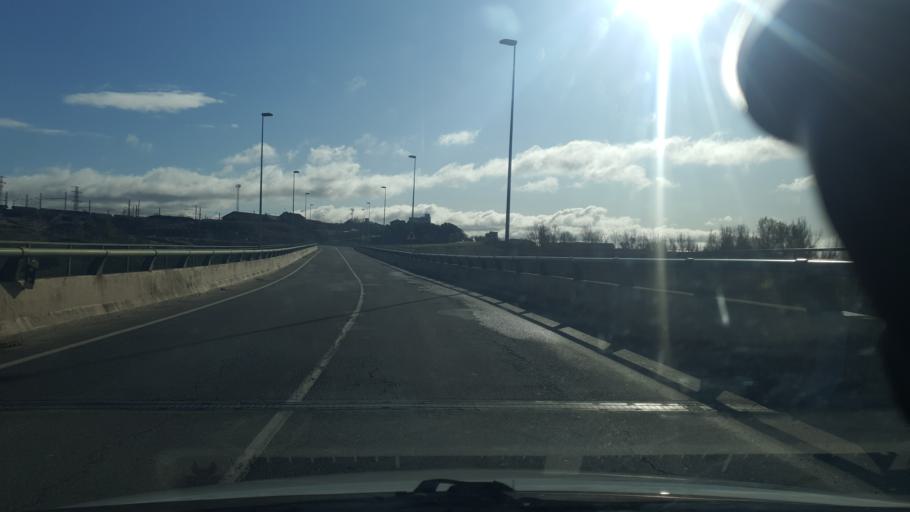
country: ES
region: Castille and Leon
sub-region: Provincia de Avila
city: Arevalo
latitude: 41.0505
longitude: -4.7069
